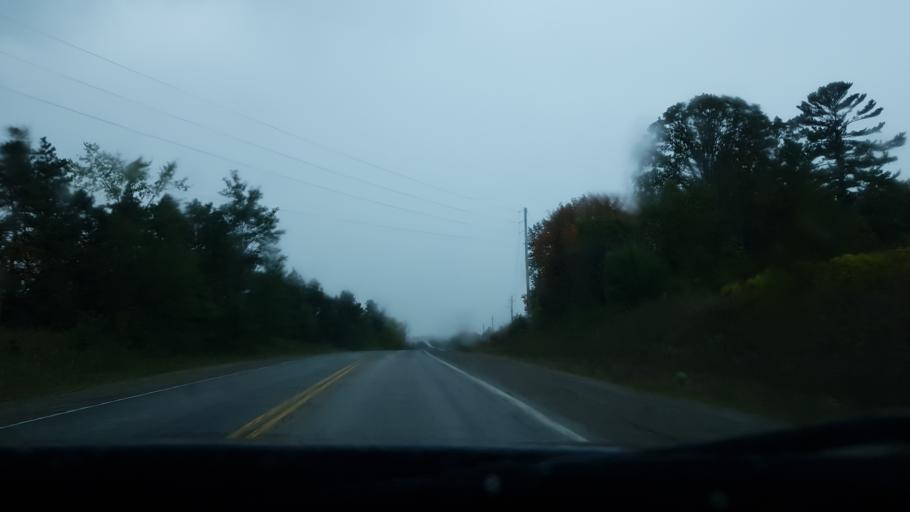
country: CA
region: Ontario
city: Omemee
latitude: 44.3498
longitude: -78.5429
